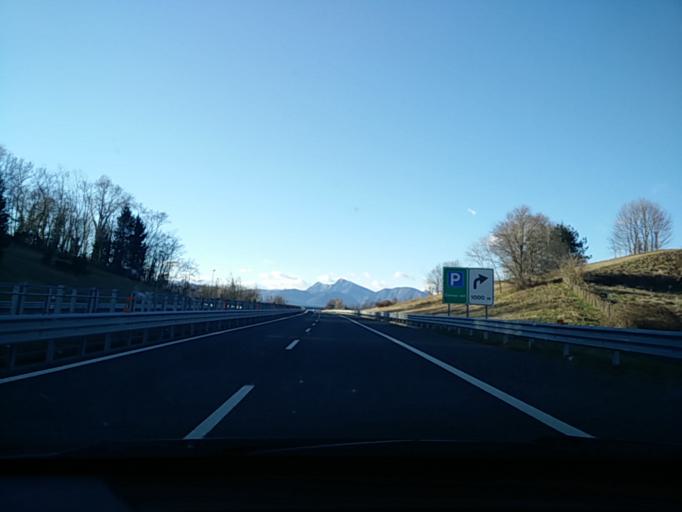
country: IT
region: Friuli Venezia Giulia
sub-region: Provincia di Udine
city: Collofedo di Monte Albano
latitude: 46.1665
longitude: 13.1566
